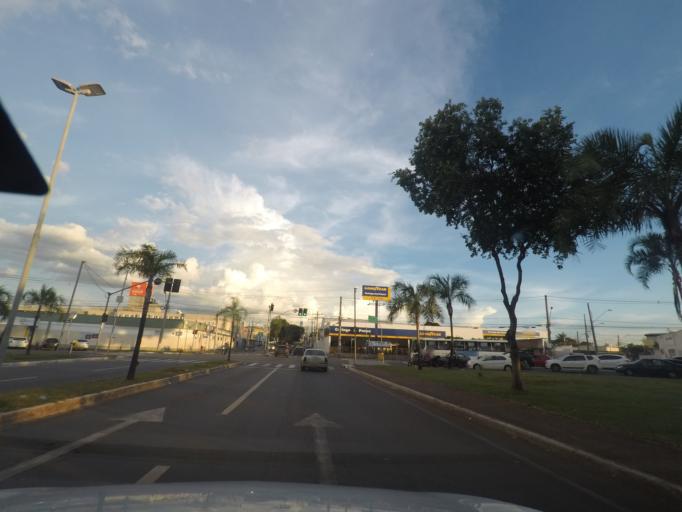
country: BR
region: Goias
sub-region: Goiania
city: Goiania
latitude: -16.6788
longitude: -49.2855
